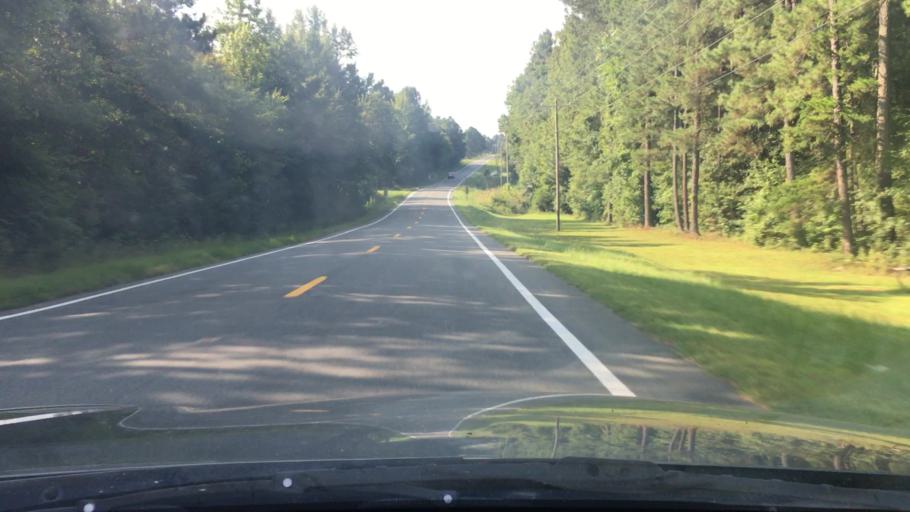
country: US
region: North Carolina
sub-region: Alamance County
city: Green Level
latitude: 36.2222
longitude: -79.3226
